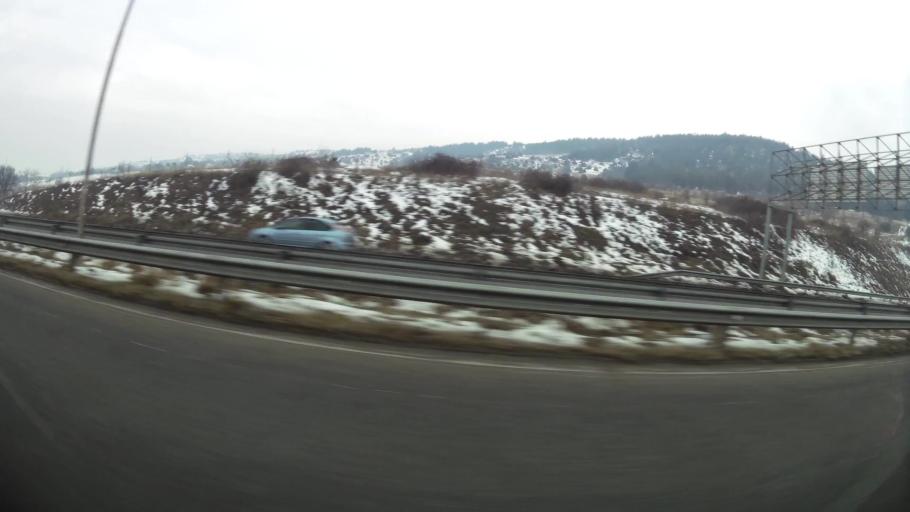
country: MK
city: Kondovo
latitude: 42.0426
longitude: 21.3376
